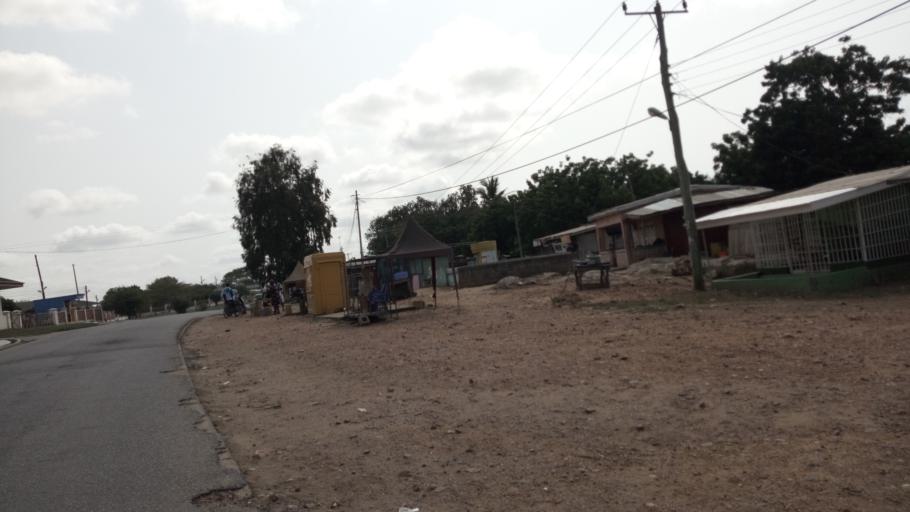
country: GH
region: Central
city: Winneba
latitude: 5.3706
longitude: -0.6426
